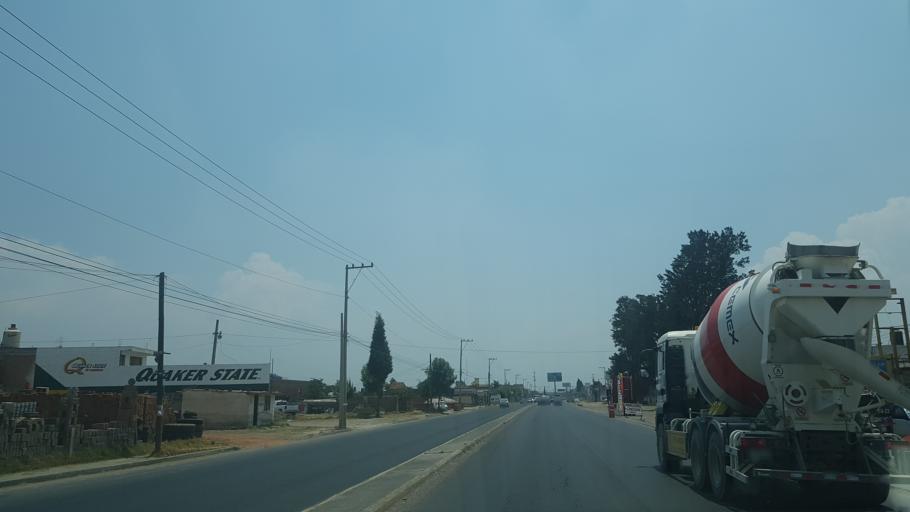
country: MX
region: Puebla
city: Cholula
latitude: 19.0756
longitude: -98.3209
